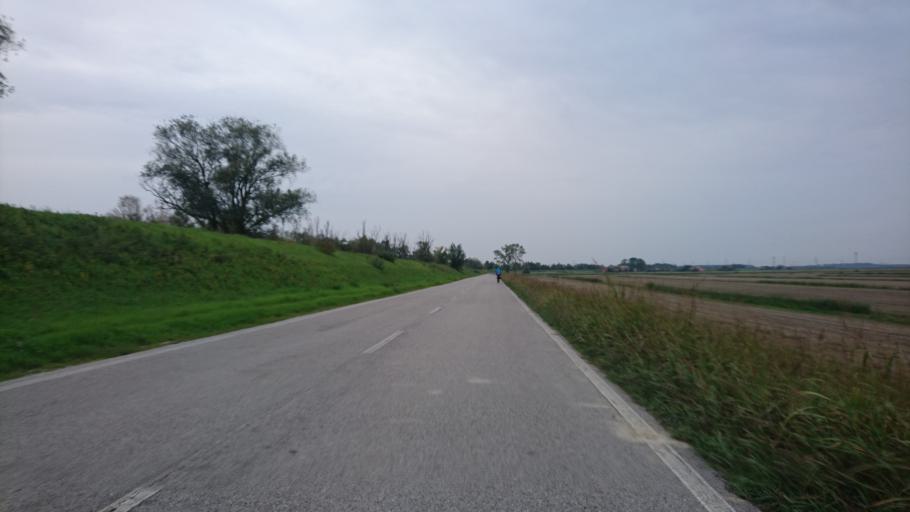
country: IT
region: Emilia-Romagna
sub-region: Provincia di Ferrara
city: Goro
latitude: 44.8791
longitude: 12.3355
